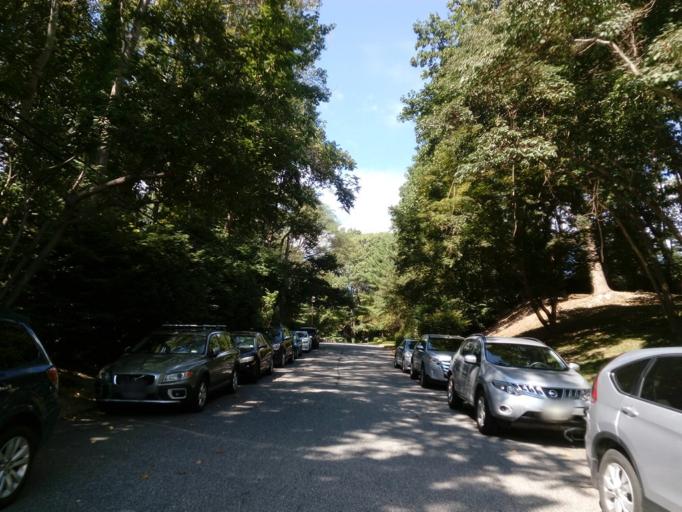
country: US
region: New York
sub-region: Nassau County
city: Oyster Bay Cove
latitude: 40.8575
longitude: -73.4974
